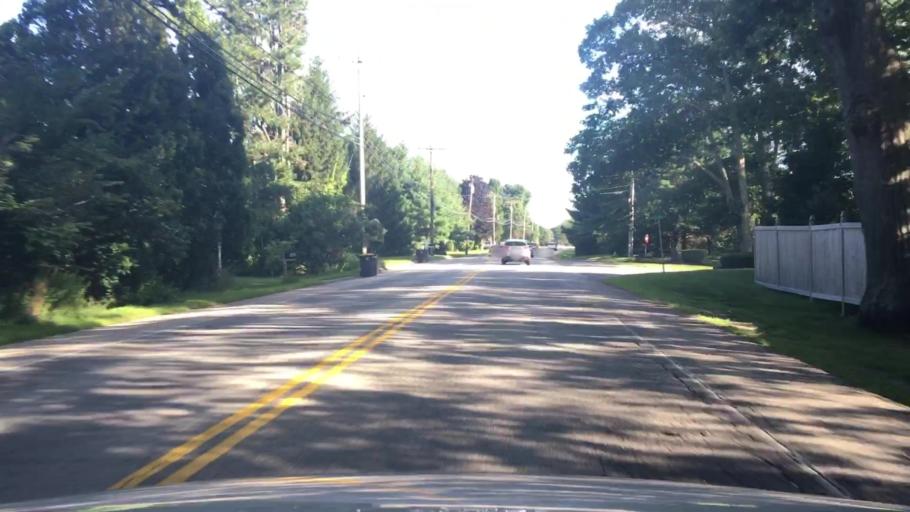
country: US
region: Maine
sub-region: Cumberland County
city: Scarborough
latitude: 43.5743
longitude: -70.3190
